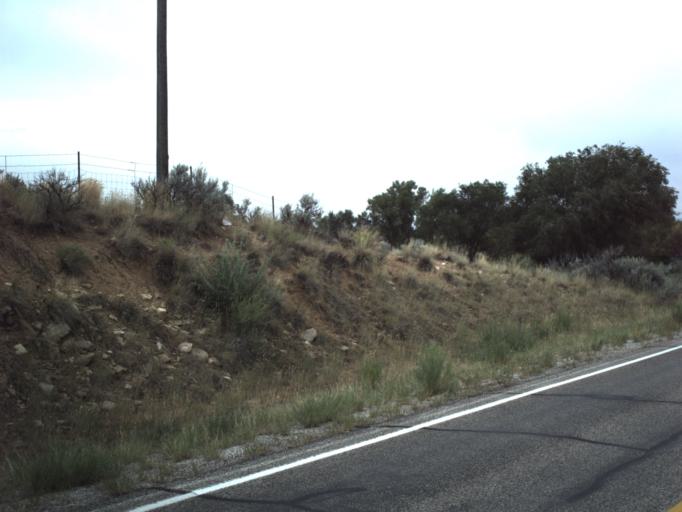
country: US
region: Utah
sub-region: Carbon County
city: East Carbon City
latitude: 39.5477
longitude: -110.4027
